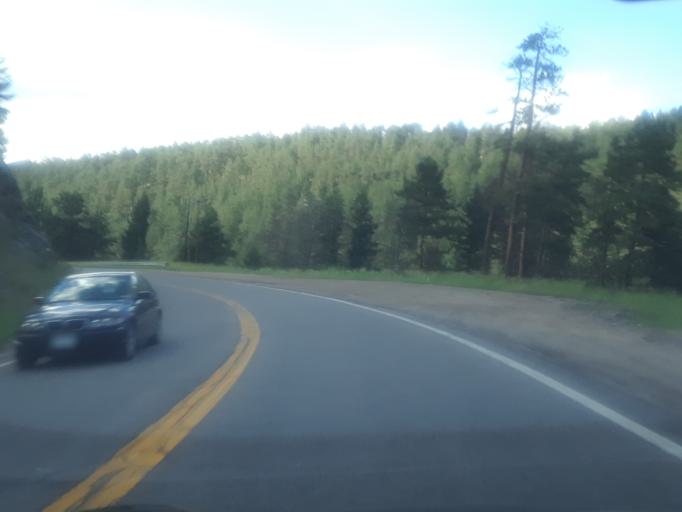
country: US
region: Colorado
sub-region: Jefferson County
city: Kittredge
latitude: 39.7149
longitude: -105.3513
